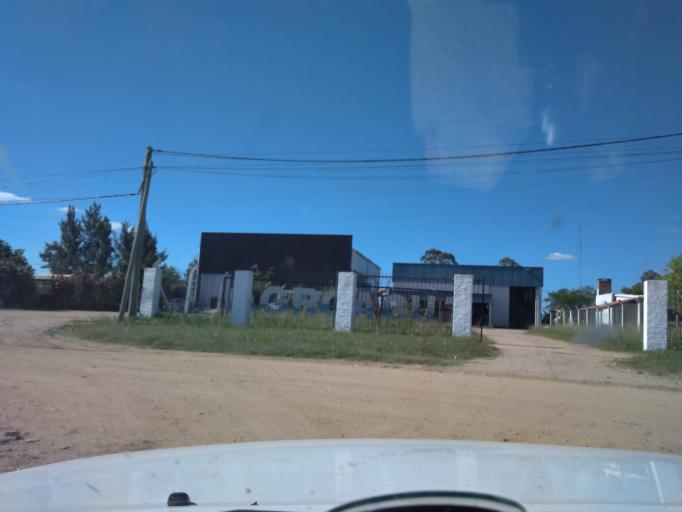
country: UY
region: Florida
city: Florida
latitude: -34.0784
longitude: -56.2223
